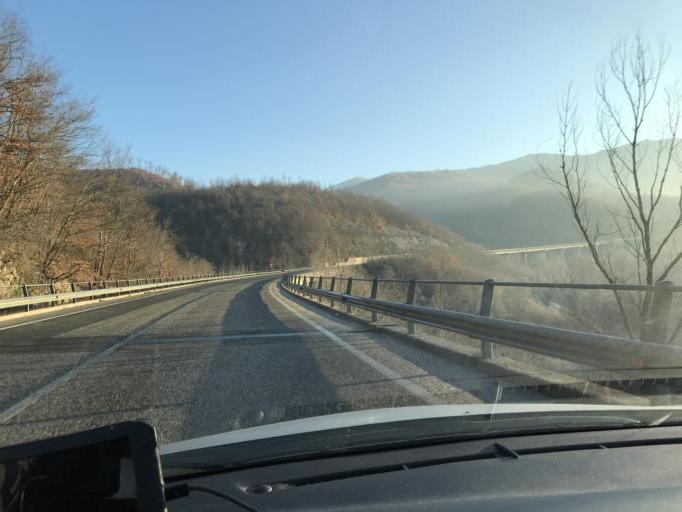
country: IT
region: Latium
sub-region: Provincia di Rieti
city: Concerviano
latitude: 42.3347
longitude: 12.9964
